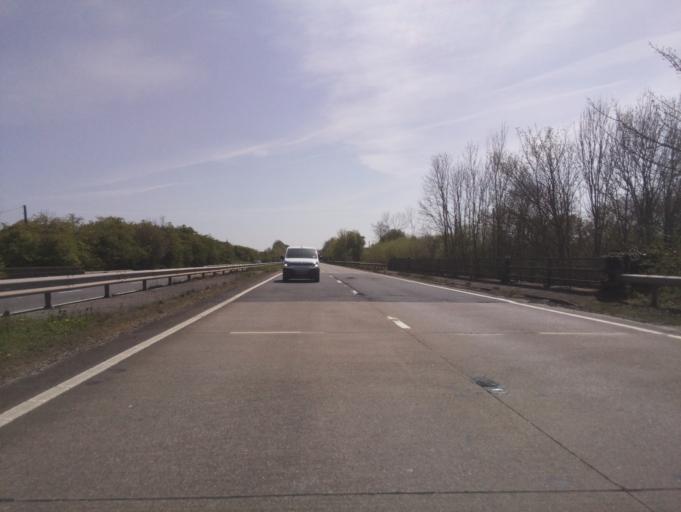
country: GB
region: Wales
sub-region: Monmouthshire
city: Abergavenny
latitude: 51.7976
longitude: -2.9982
